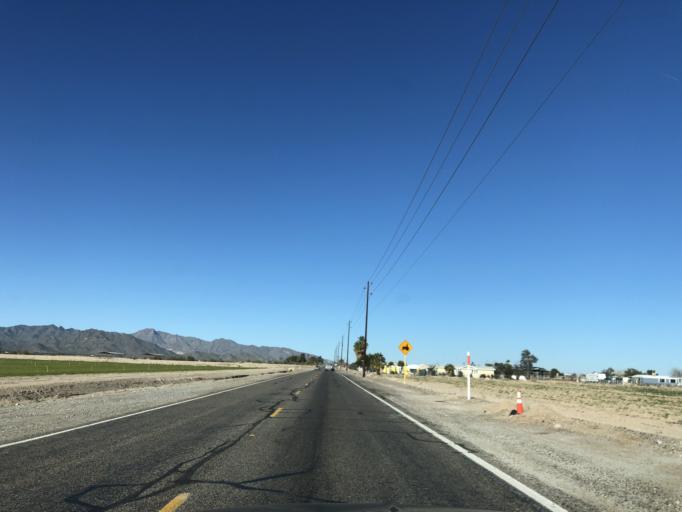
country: US
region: Arizona
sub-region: Maricopa County
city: Buckeye
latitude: 33.4229
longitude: -112.5042
